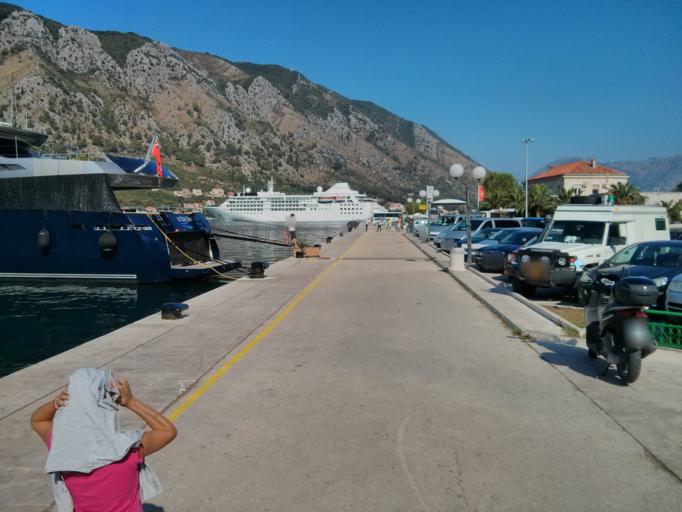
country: ME
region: Kotor
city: Kotor
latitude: 42.4247
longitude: 18.7687
